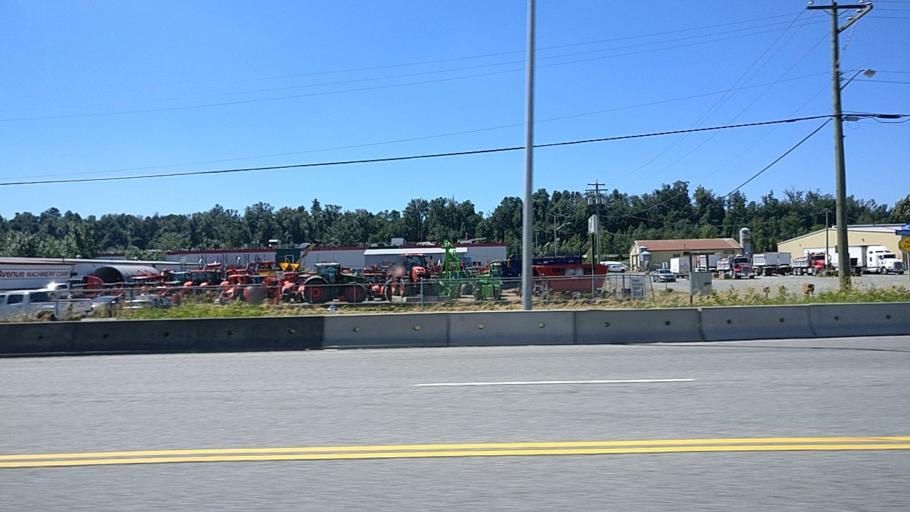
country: US
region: Washington
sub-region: Whatcom County
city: Sumas
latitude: 49.0300
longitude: -122.2655
